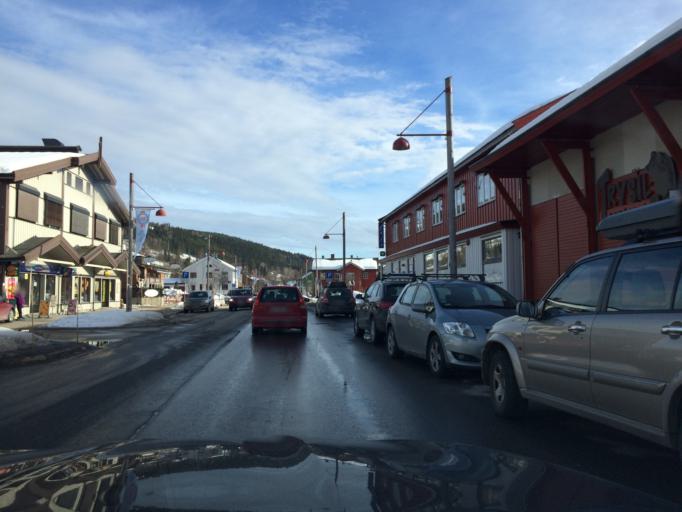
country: NO
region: Hedmark
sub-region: Trysil
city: Innbygda
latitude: 61.3159
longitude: 12.2618
